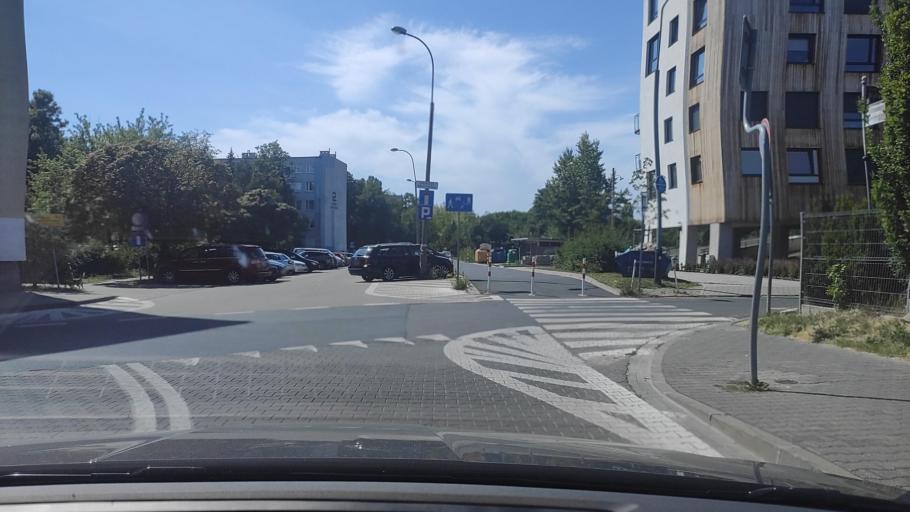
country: PL
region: Greater Poland Voivodeship
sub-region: Poznan
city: Poznan
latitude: 52.4326
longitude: 16.9336
